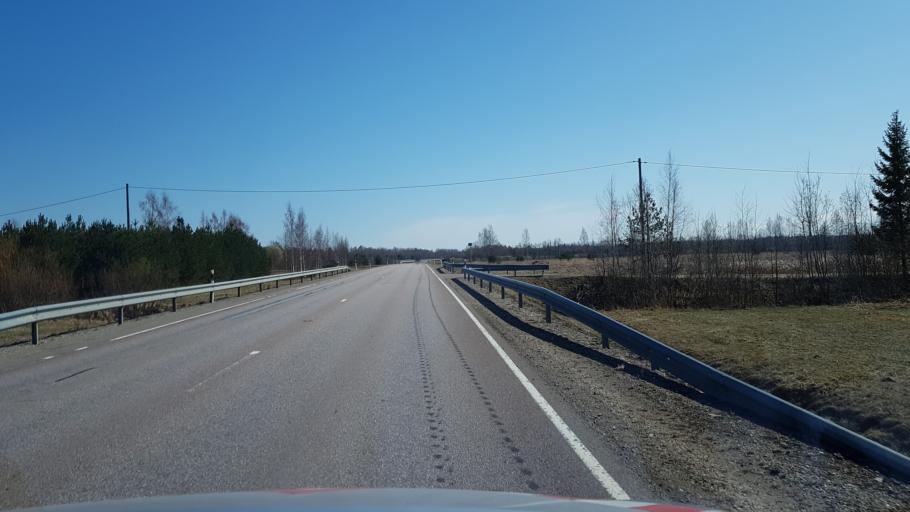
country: EE
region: Jogevamaa
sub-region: Mustvee linn
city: Mustvee
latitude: 58.8055
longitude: 26.9382
